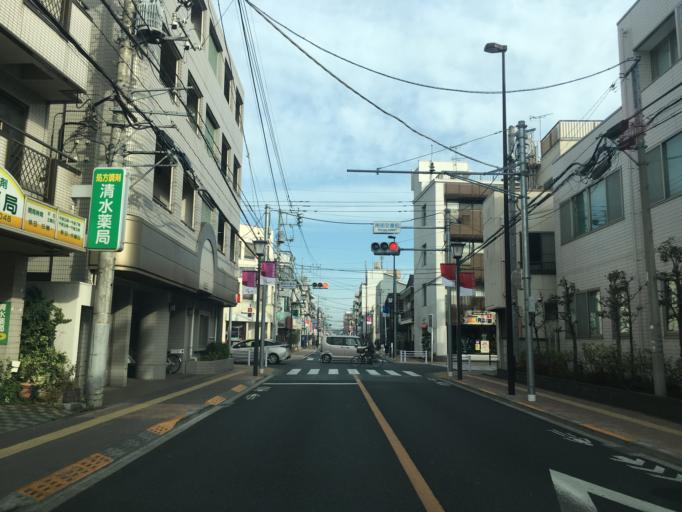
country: JP
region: Tokyo
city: Higashimurayama-shi
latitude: 35.7389
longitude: 139.4324
